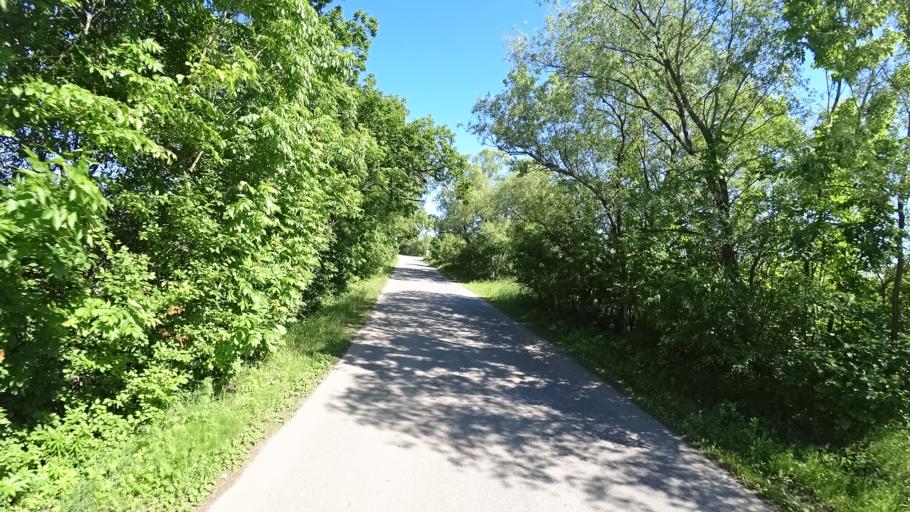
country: RU
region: Khabarovsk Krai
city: Khor
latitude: 47.8898
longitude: 135.0237
